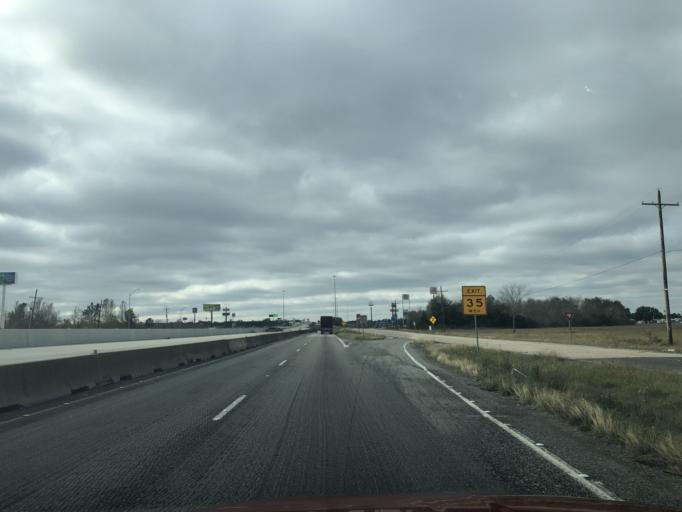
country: US
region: Texas
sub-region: Chambers County
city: Winnie
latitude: 29.8382
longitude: -94.3800
